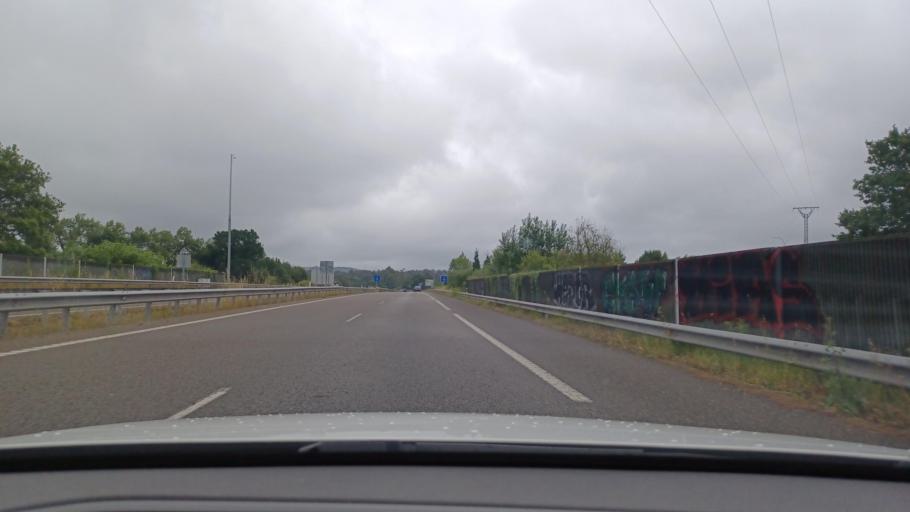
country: ES
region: Asturias
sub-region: Province of Asturias
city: Lugones
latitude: 43.4380
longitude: -5.8108
